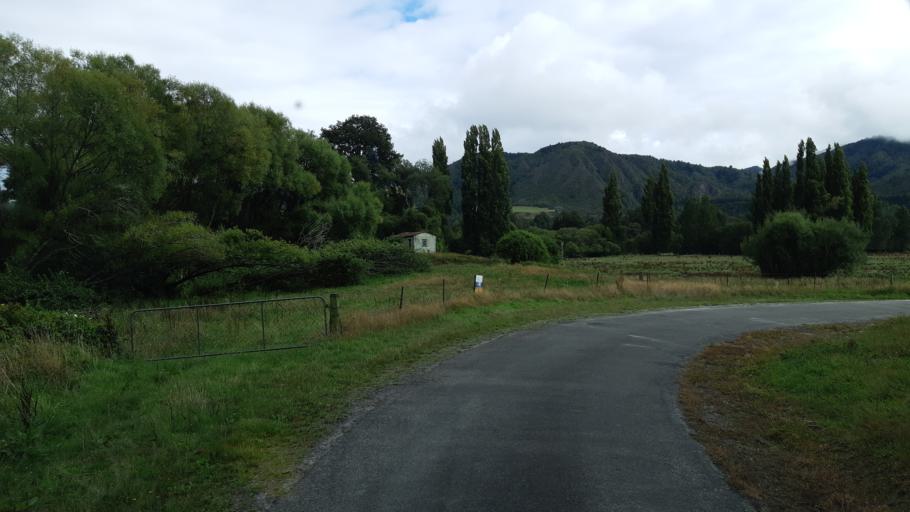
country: NZ
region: West Coast
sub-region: Buller District
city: Westport
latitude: -41.7816
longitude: 172.2751
